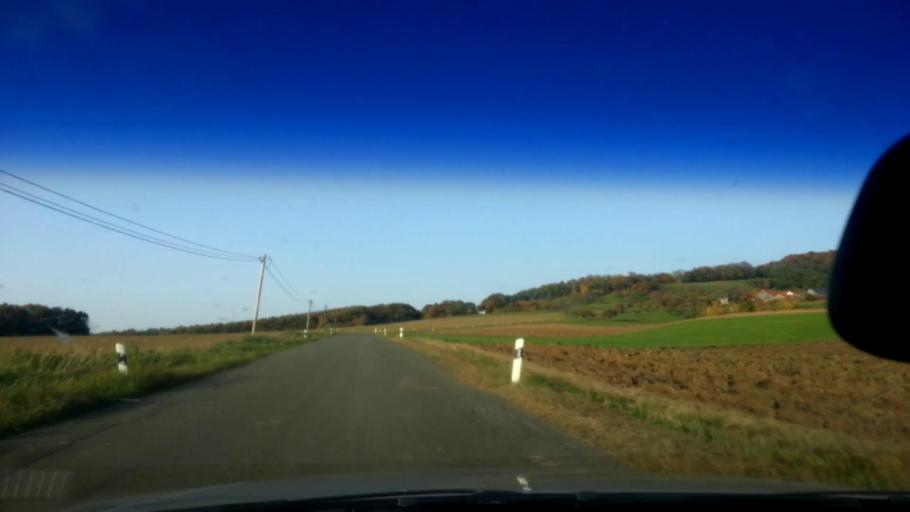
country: DE
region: Bavaria
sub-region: Upper Franconia
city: Schesslitz
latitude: 50.0125
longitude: 11.0200
